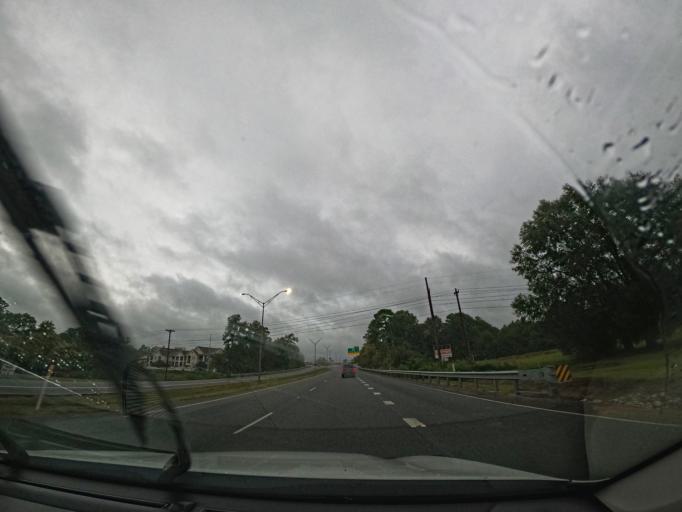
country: US
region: Texas
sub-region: Angelina County
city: Lufkin
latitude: 31.2932
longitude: -94.7288
